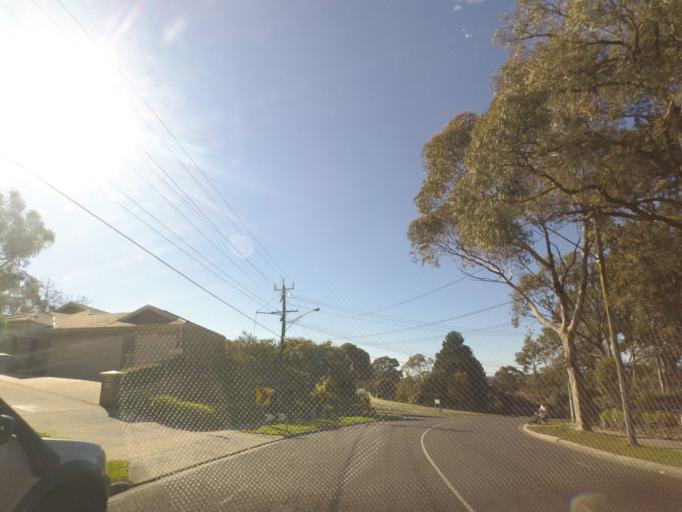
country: AU
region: Victoria
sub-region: Maroondah
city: Croydon Hills
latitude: -37.7780
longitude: 145.2566
